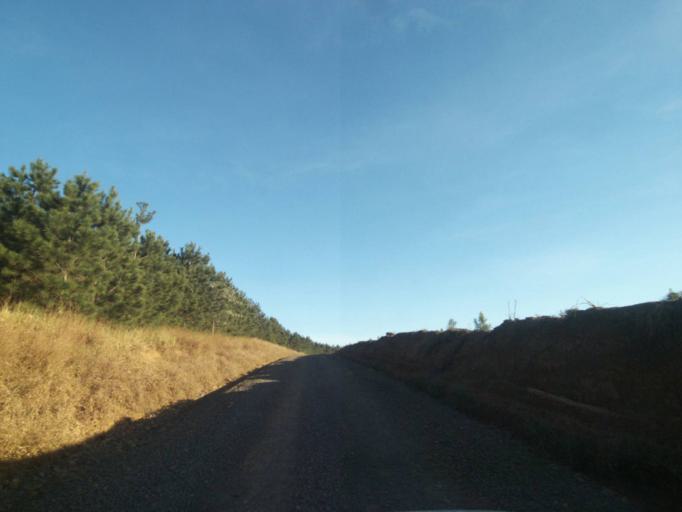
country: BR
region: Parana
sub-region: Telemaco Borba
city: Telemaco Borba
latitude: -24.4522
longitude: -50.5998
